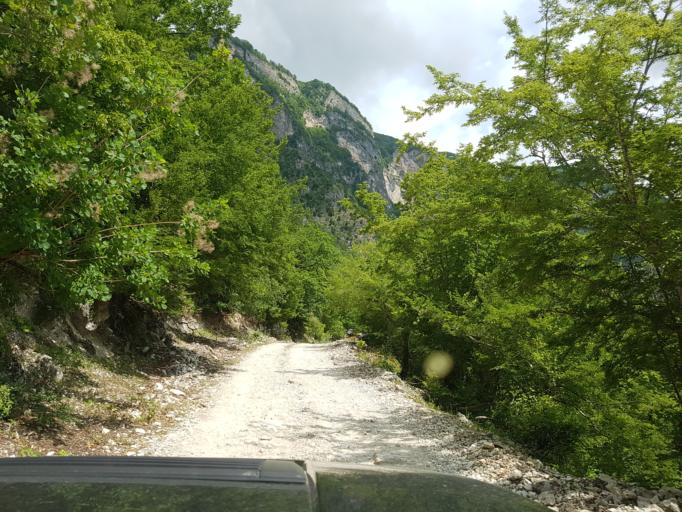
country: GE
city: Tqibuli
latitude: 42.5186
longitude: 42.8040
